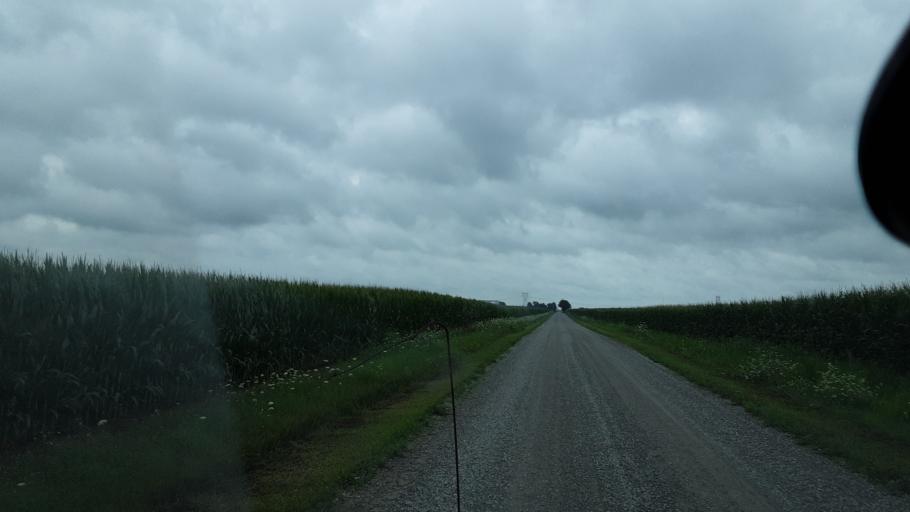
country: US
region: Indiana
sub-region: Wells County
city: Bluffton
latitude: 40.7697
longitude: -85.0710
